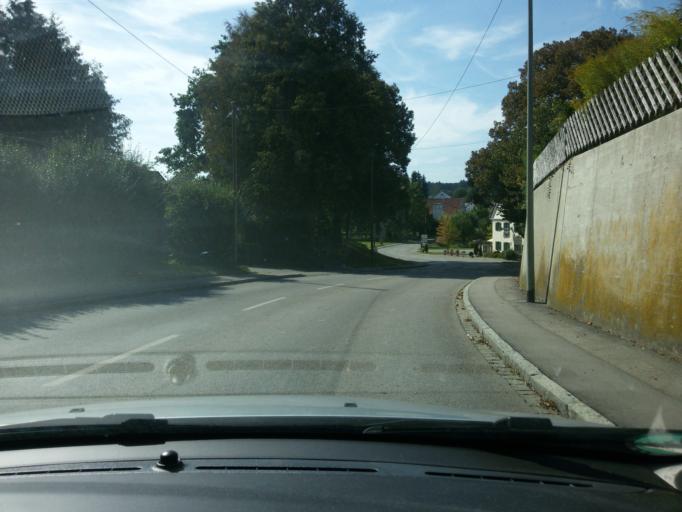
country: DE
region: Bavaria
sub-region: Swabia
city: Fischach
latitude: 48.2499
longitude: 10.6984
